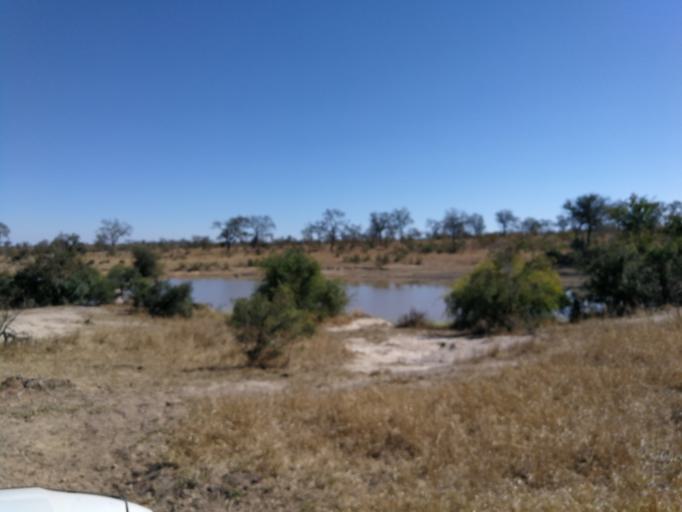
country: ZA
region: Limpopo
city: Thulamahashi
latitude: -24.8564
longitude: 31.7536
